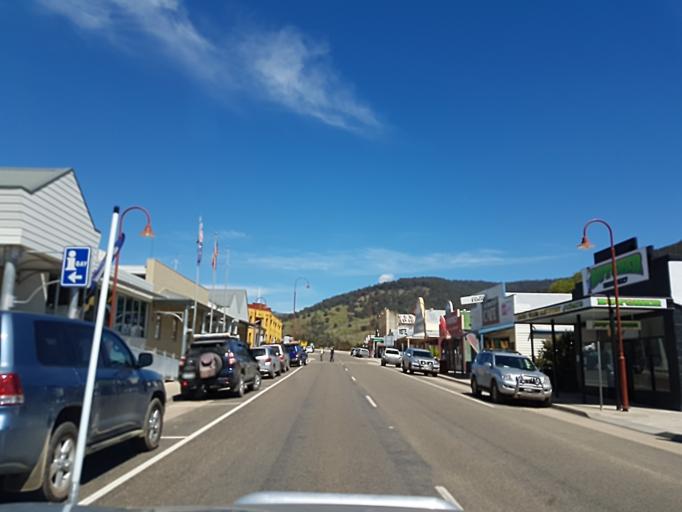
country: AU
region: Victoria
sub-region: Alpine
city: Mount Beauty
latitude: -37.1005
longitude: 147.5922
